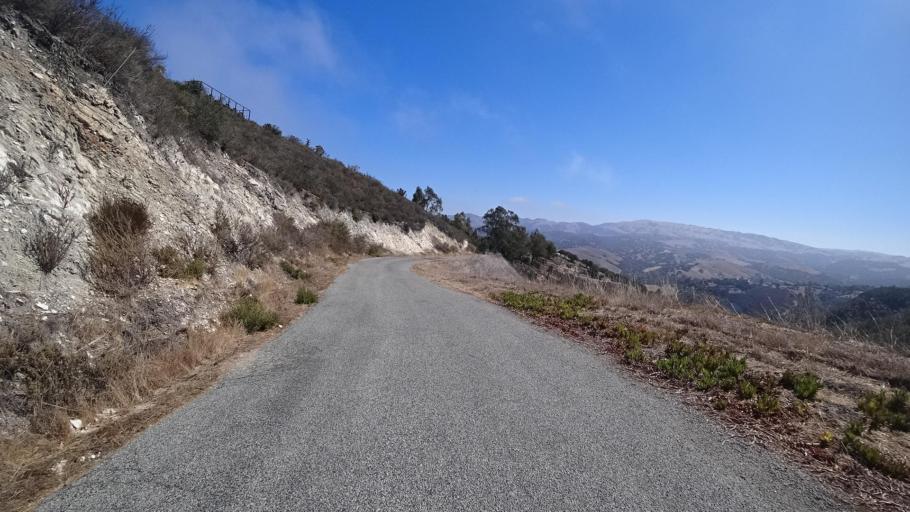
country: US
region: California
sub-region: Monterey County
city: Carmel Valley Village
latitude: 36.5489
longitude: -121.7454
